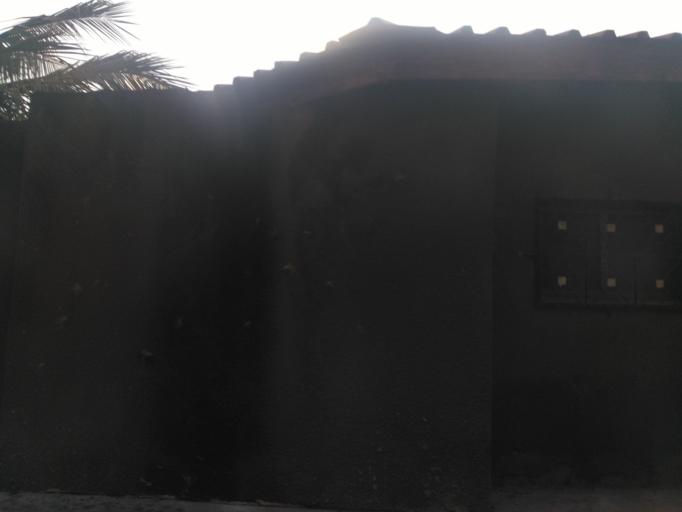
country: TZ
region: Zanzibar Urban/West
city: Zanzibar
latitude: -6.1684
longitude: 39.1985
